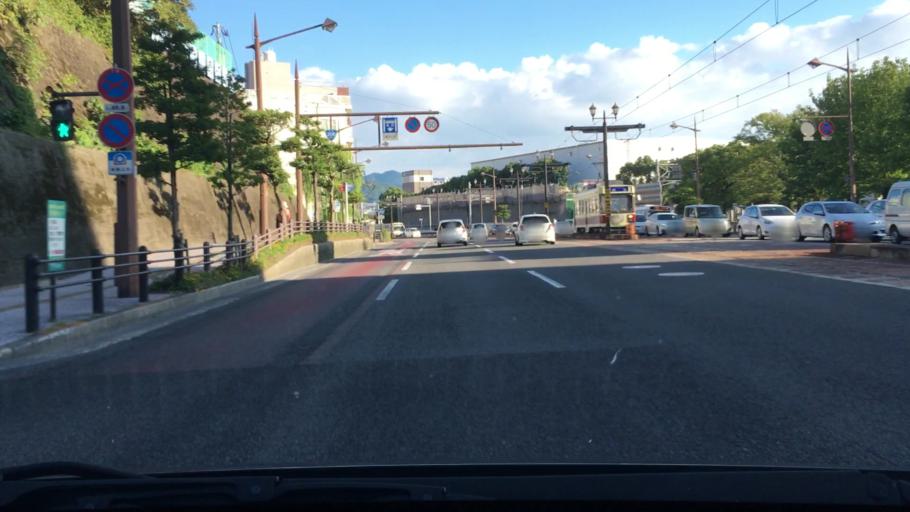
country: JP
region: Nagasaki
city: Nagasaki-shi
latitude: 32.7610
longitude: 129.8660
